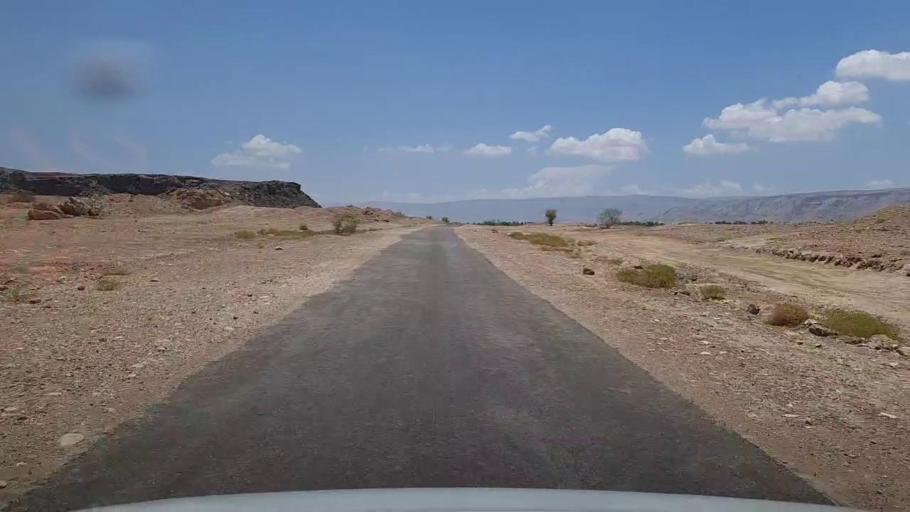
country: PK
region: Sindh
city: Bhan
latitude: 26.2944
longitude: 67.5339
